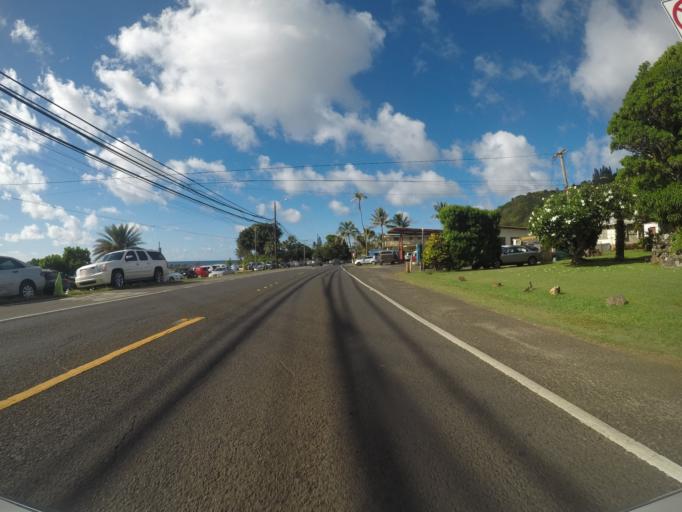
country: US
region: Hawaii
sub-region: Honolulu County
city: Pupukea
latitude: 21.6503
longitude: -158.0619
